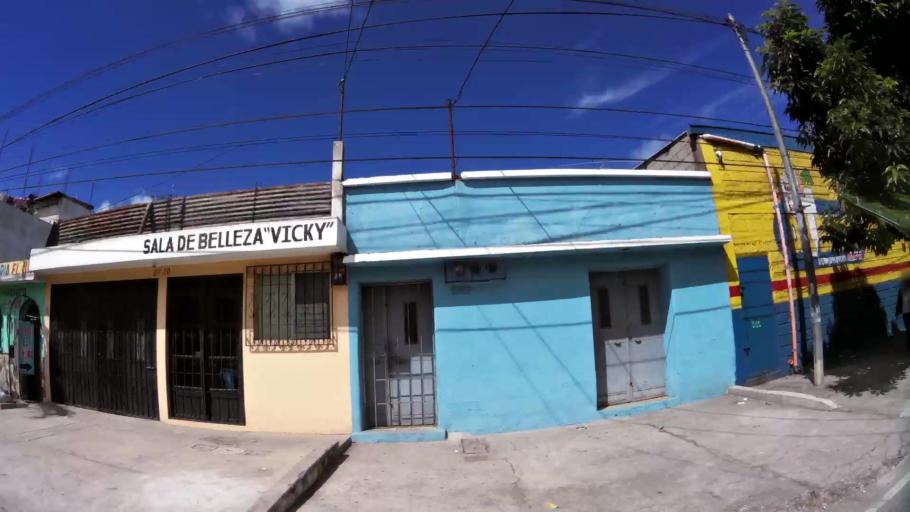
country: GT
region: Guatemala
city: Guatemala City
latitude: 14.5963
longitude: -90.5474
